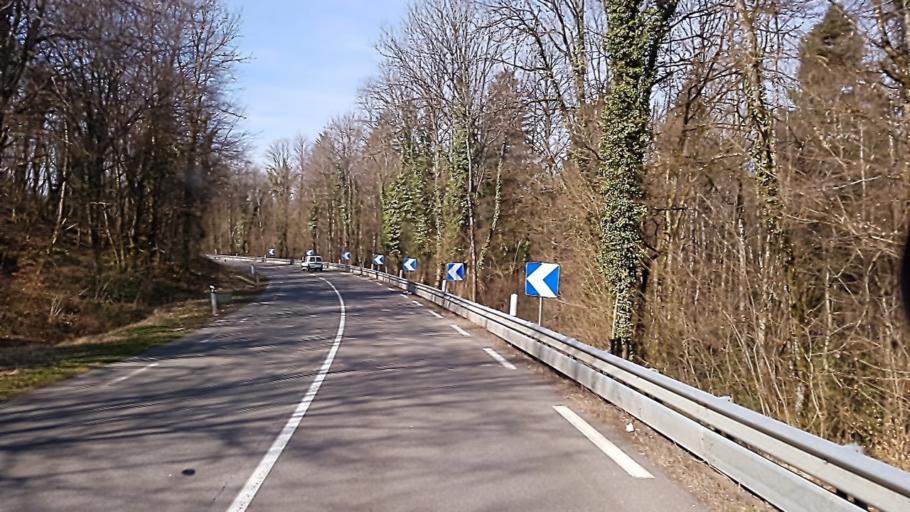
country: FR
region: Franche-Comte
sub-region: Departement du Jura
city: Poligny
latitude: 46.8169
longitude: 5.7721
